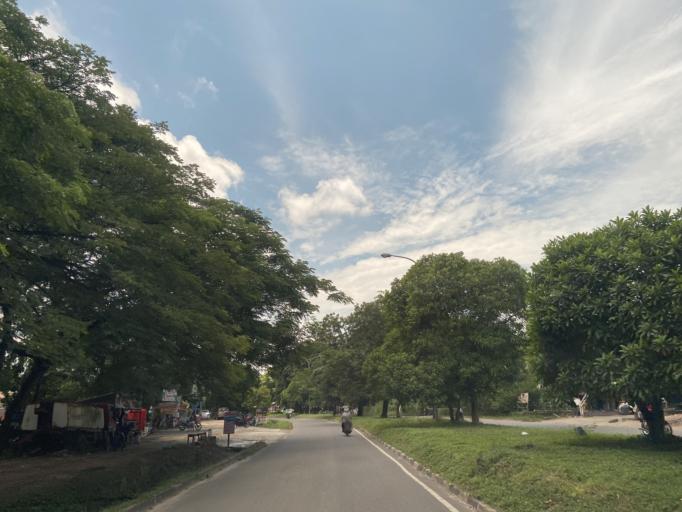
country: SG
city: Singapore
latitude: 1.1584
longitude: 104.0238
